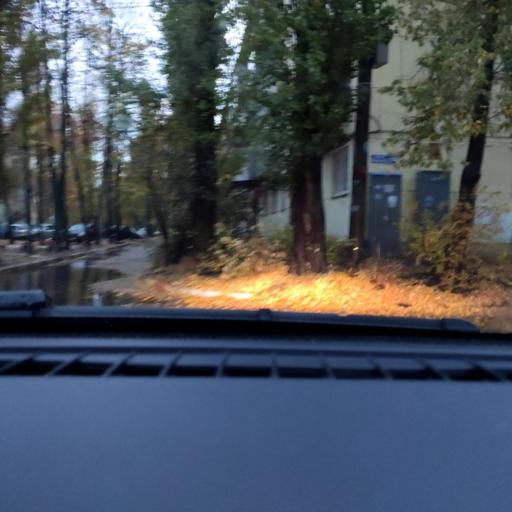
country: RU
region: Voronezj
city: Voronezh
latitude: 51.6914
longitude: 39.2657
